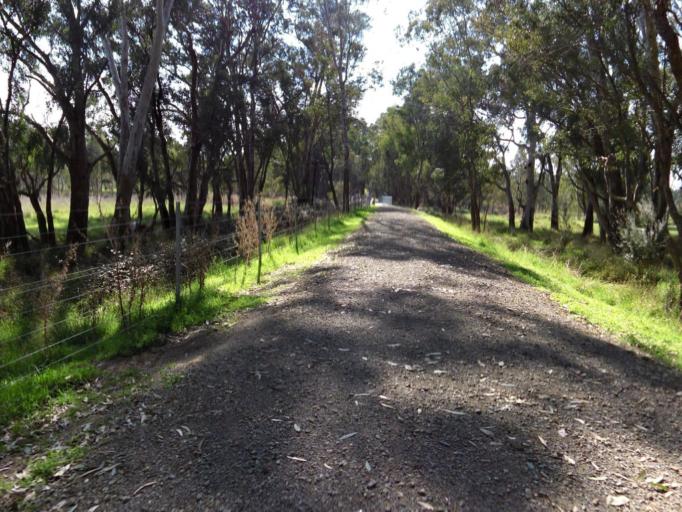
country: AU
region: Victoria
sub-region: Murrindindi
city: Alexandra
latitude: -37.1556
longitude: 145.5742
